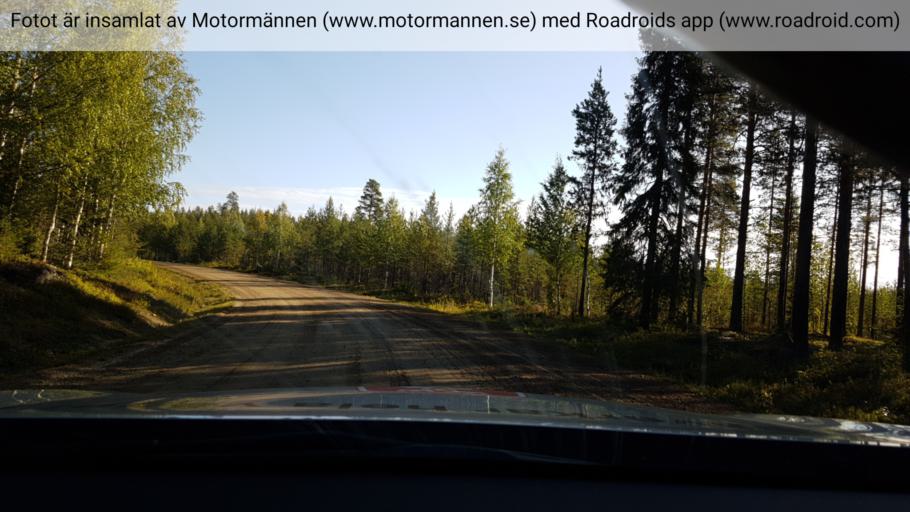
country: SE
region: Vaesterbotten
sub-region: Norsjo Kommun
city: Norsjoe
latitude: 64.5913
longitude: 19.3524
